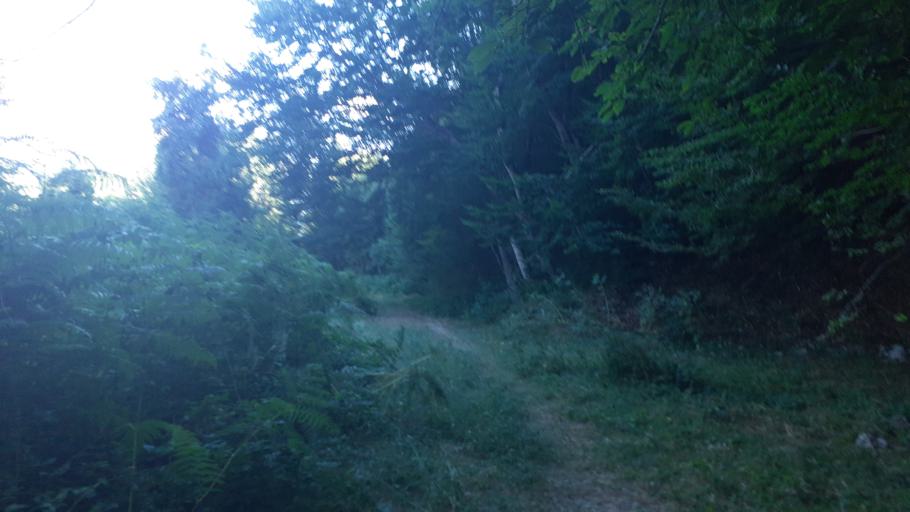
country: IT
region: Abruzzo
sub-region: Provincia di Pescara
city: Sant'Eufemia a Maiella
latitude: 42.1070
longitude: 14.0022
